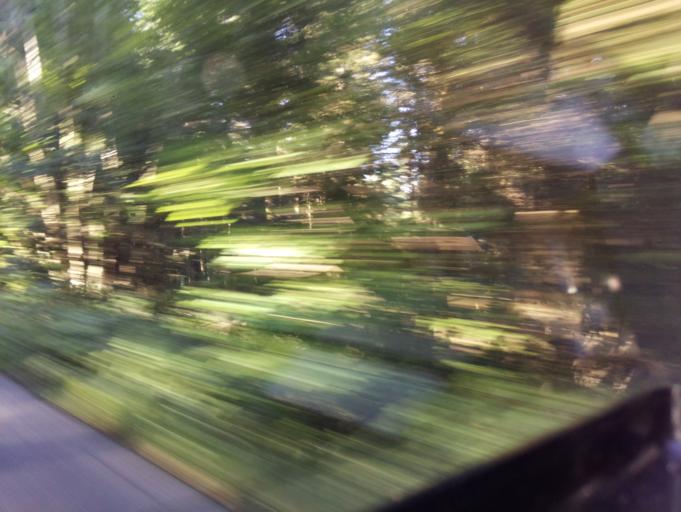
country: GB
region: Wales
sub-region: Monmouthshire
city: Tintern
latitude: 51.6680
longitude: -2.7487
